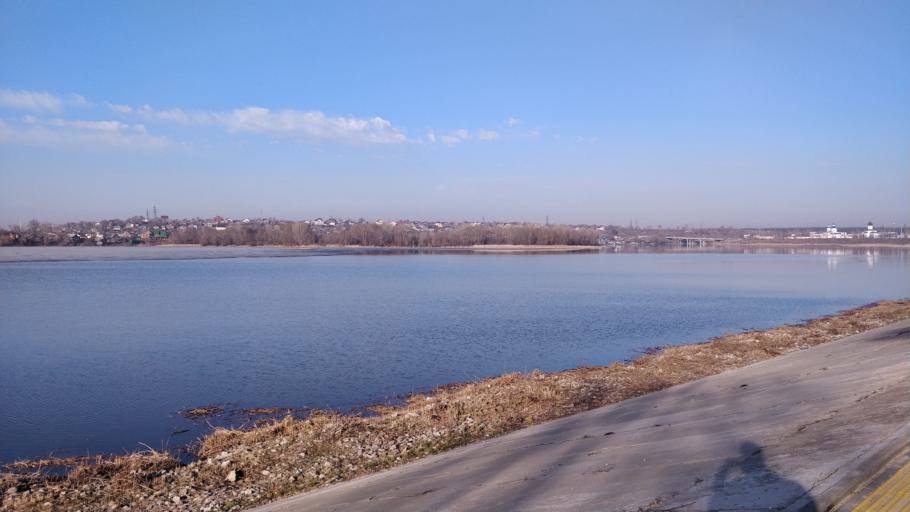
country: RU
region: Samara
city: Syzran'
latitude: 53.1447
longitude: 48.4579
